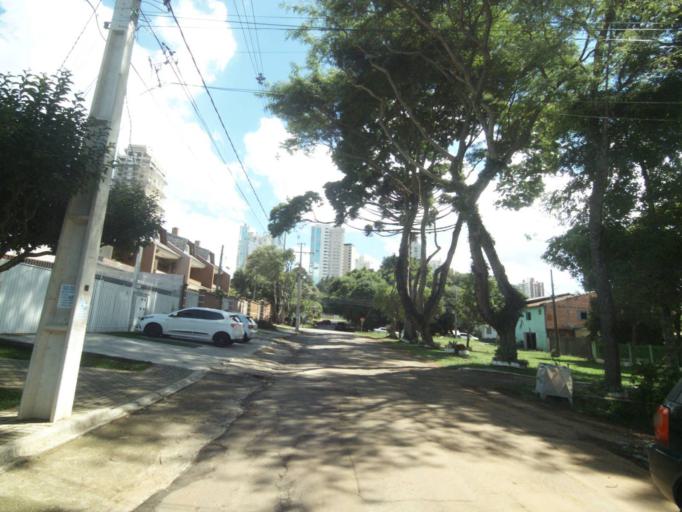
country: BR
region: Parana
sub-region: Curitiba
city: Curitiba
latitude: -25.4359
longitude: -49.3367
